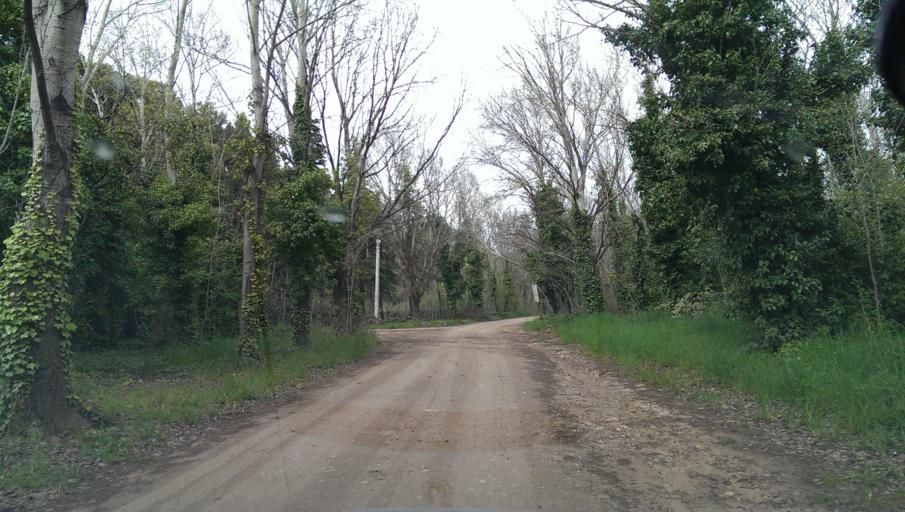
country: AR
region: Buenos Aires
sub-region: Partido de Tornquist
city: Tornquist
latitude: -38.0752
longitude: -61.9280
